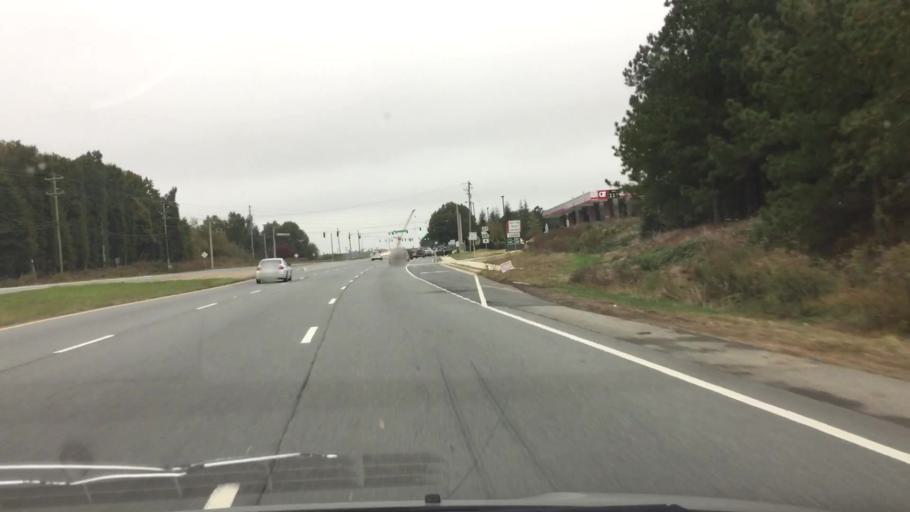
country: US
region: Georgia
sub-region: Fulton County
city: Milton
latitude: 34.1197
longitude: -84.2232
